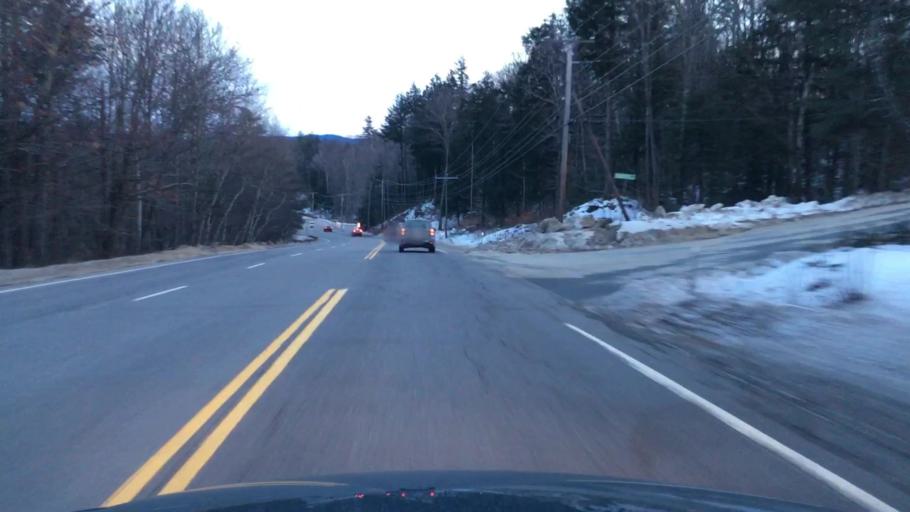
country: US
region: New Hampshire
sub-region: Merrimack County
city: Newbury
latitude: 43.3126
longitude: -72.0271
